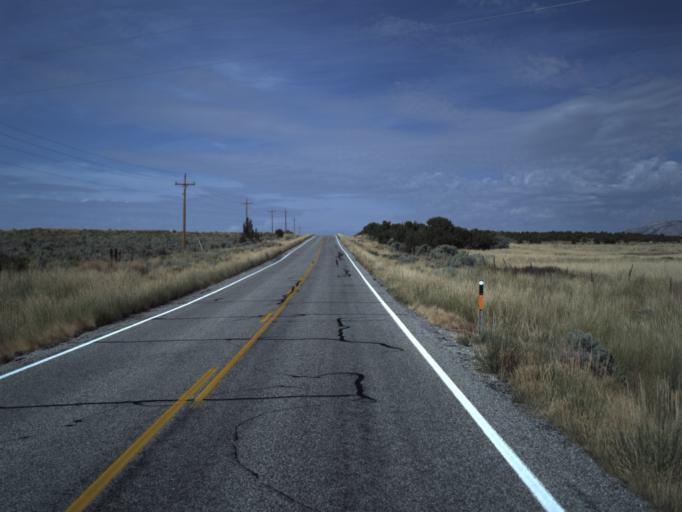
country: US
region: Idaho
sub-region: Cassia County
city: Burley
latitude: 41.8174
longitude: -113.2528
